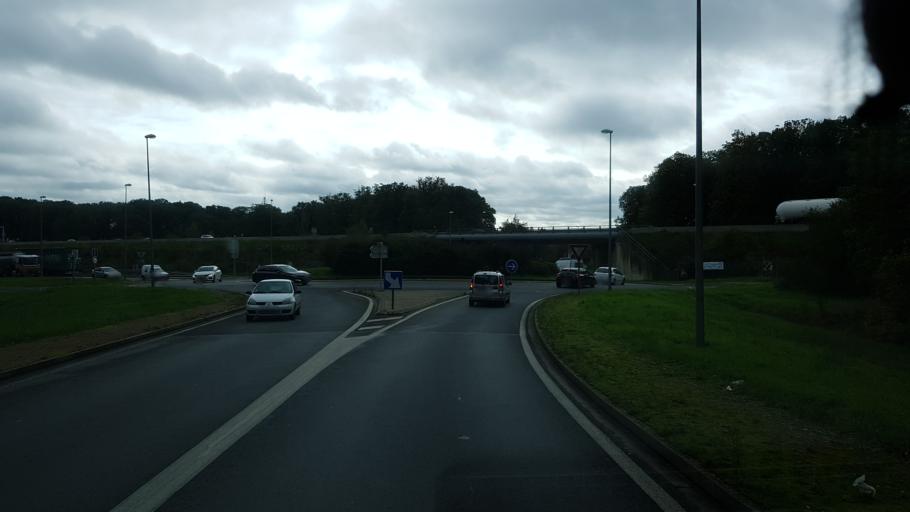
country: FR
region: Centre
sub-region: Departement du Cher
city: Vierzon
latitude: 47.2495
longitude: 2.0605
